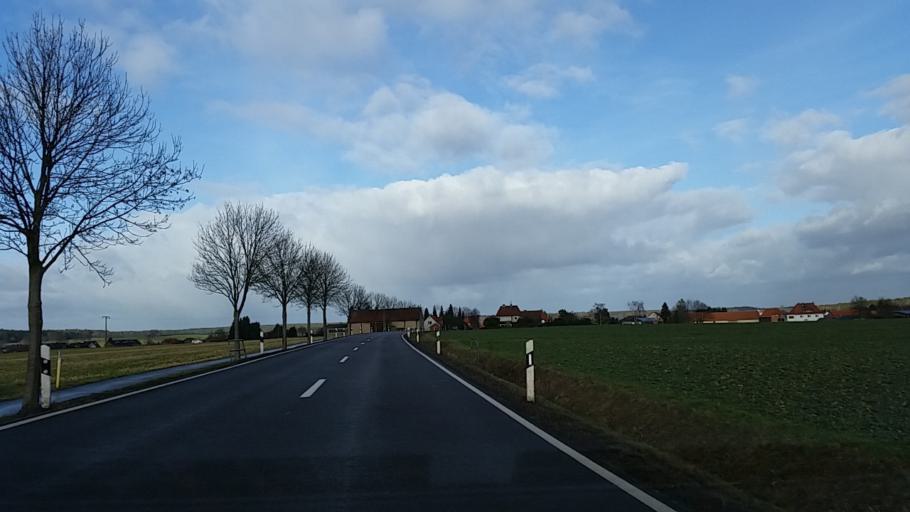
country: DE
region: Lower Saxony
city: Gross Twulpstedt
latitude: 52.3807
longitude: 10.9196
